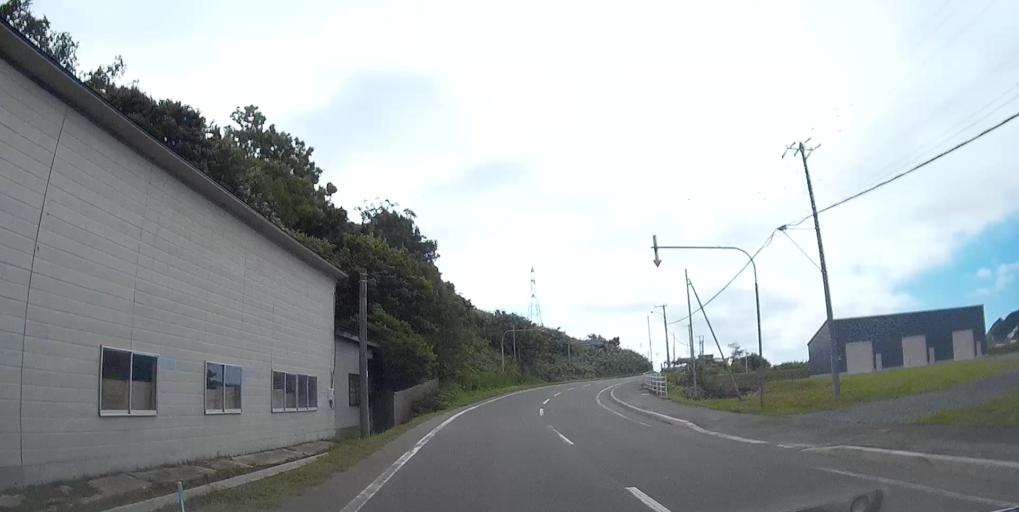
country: JP
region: Hokkaido
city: Kamiiso
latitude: 41.9715
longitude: 140.1474
